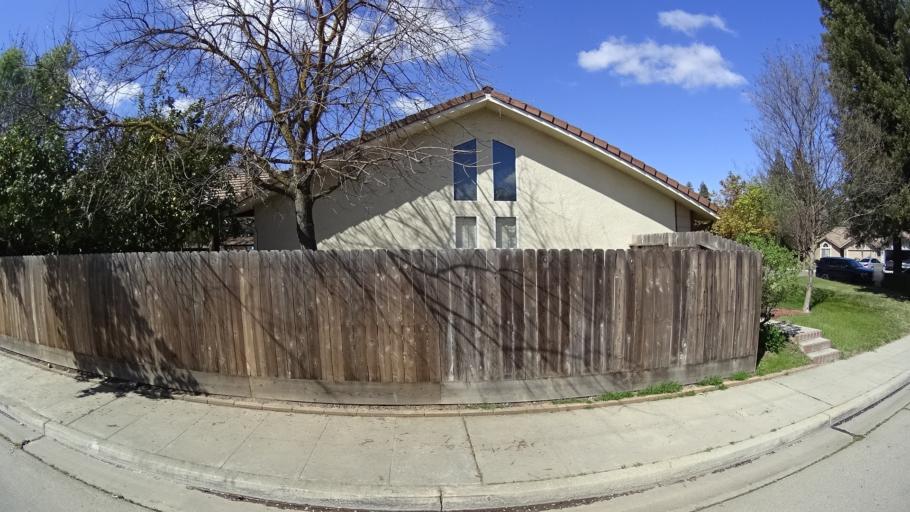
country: US
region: California
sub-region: Fresno County
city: West Park
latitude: 36.8218
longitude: -119.8902
